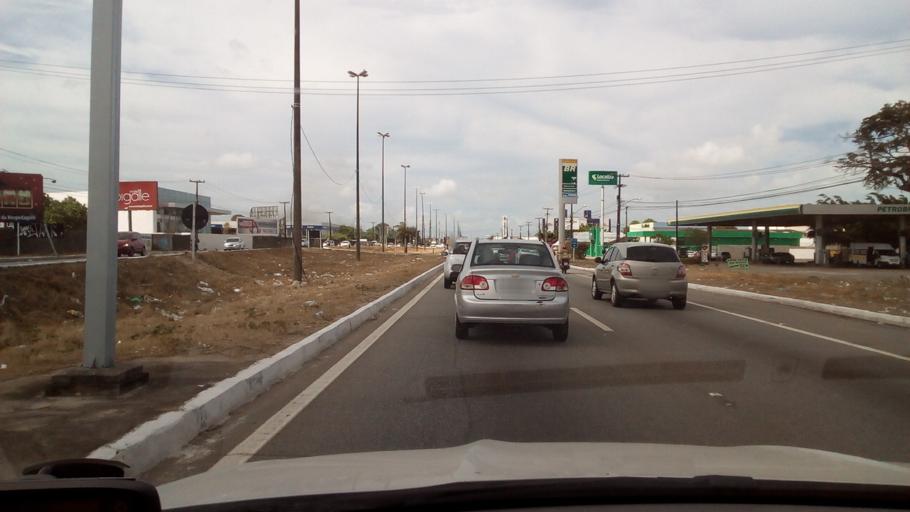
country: BR
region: Paraiba
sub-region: Joao Pessoa
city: Joao Pessoa
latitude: -7.0908
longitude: -34.8483
